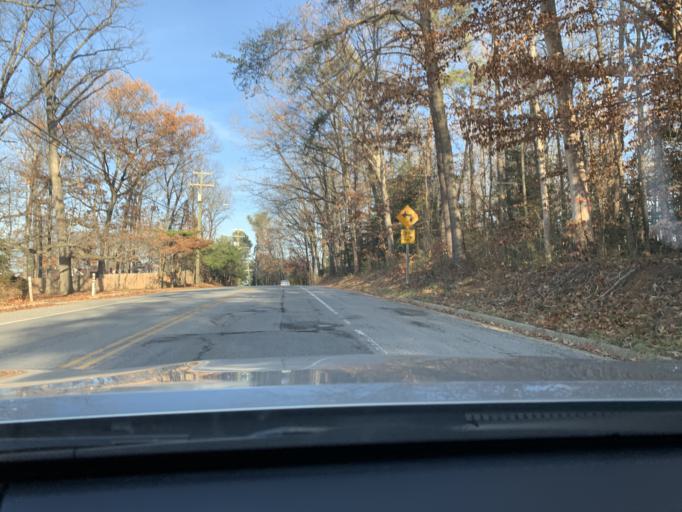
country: US
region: Virginia
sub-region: Fairfax County
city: Lake Barcroft
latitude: 38.8509
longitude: -77.1712
